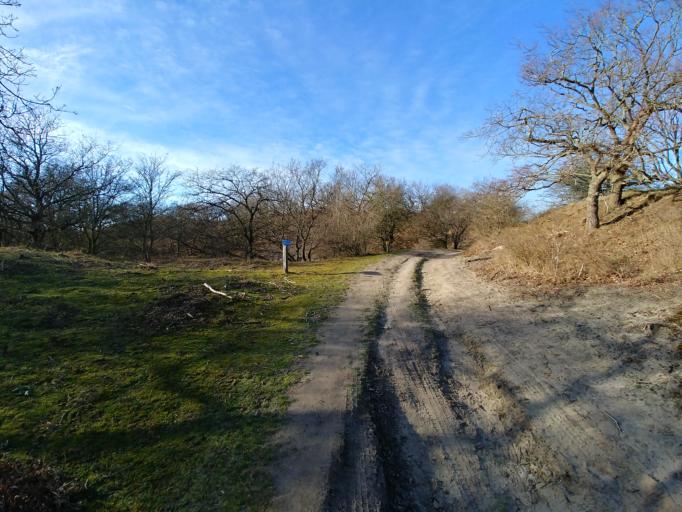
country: NL
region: South Holland
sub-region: Gemeente Den Haag
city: Scheveningen
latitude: 52.1288
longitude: 4.3266
